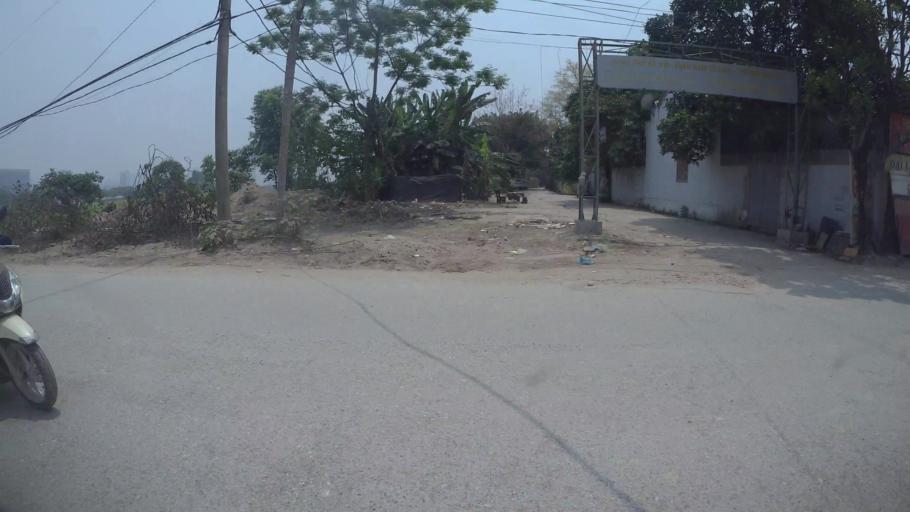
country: VN
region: Ha Noi
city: Ha Dong
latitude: 21.0017
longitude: 105.7662
